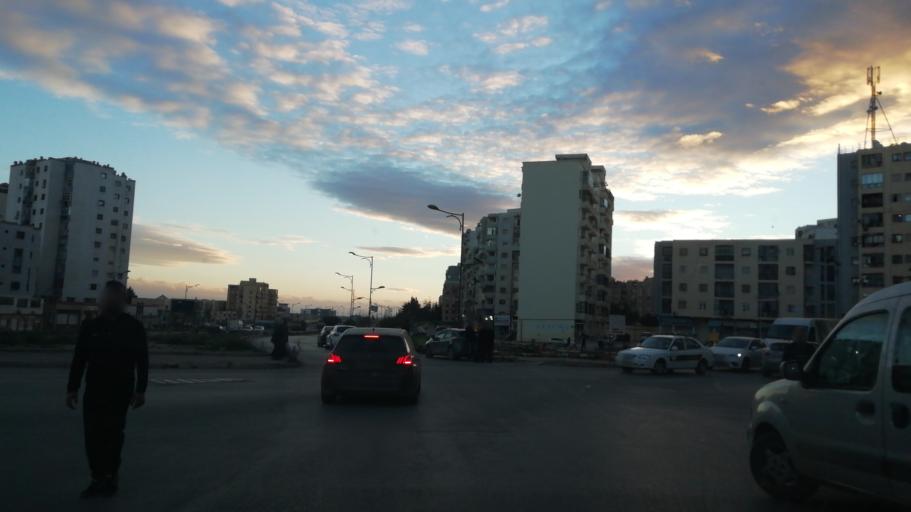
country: DZ
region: Oran
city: Bir el Djir
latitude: 35.6986
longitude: -0.5641
